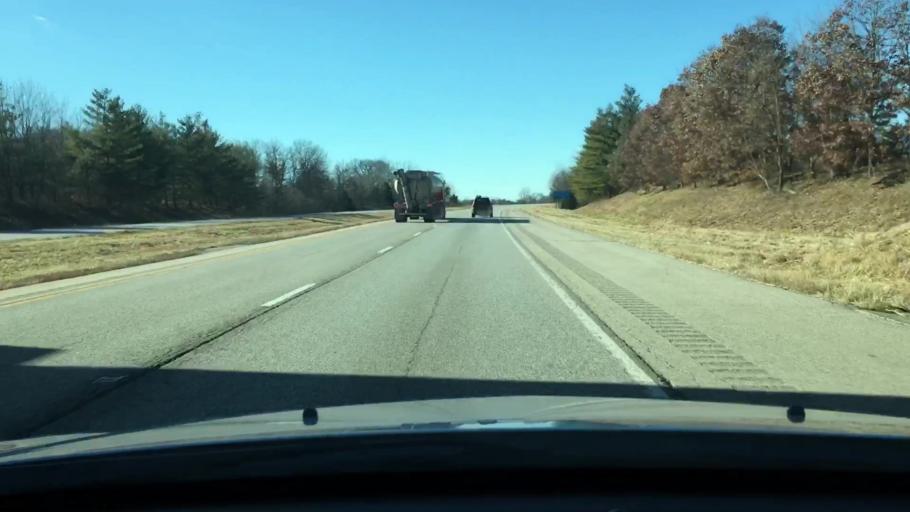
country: US
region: Illinois
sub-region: Pike County
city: Griggsville
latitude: 39.6748
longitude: -90.7424
